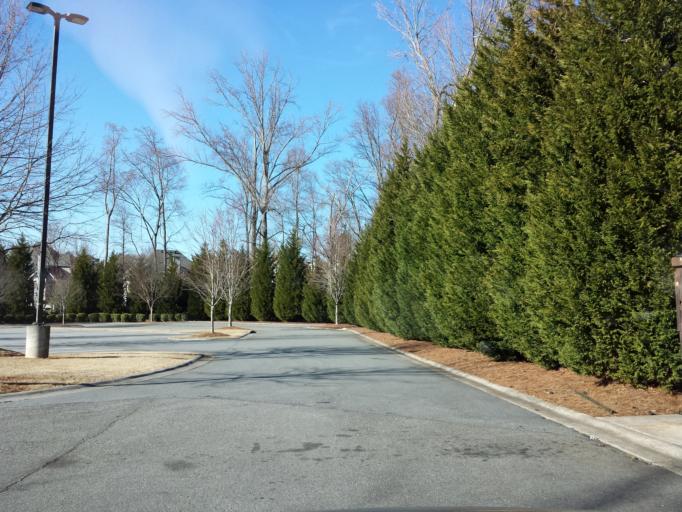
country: US
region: Georgia
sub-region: Cobb County
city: Kennesaw
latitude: 33.9746
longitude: -84.6087
